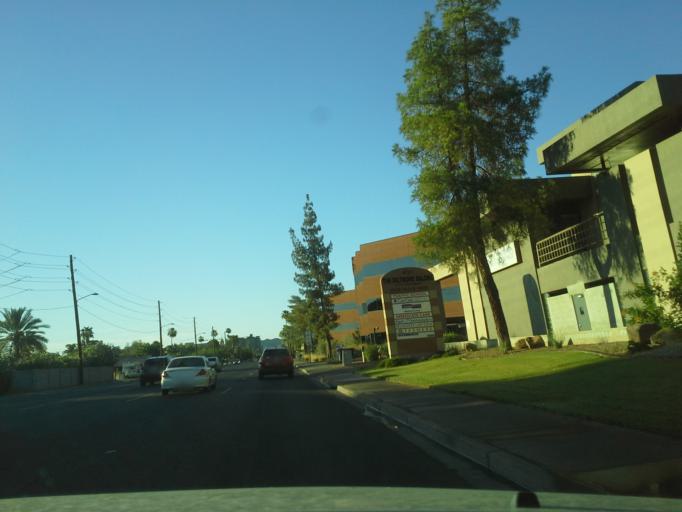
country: US
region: Arizona
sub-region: Maricopa County
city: Phoenix
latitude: 33.4957
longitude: -112.0301
